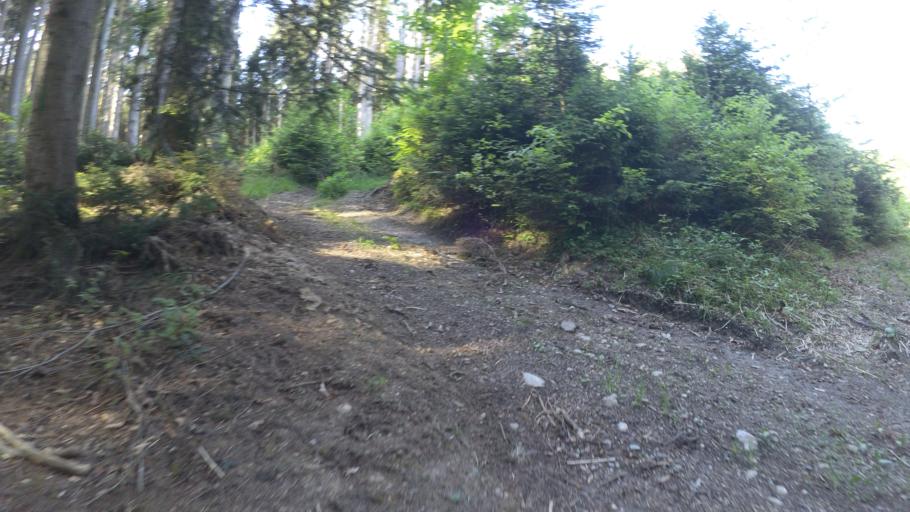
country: DE
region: Bavaria
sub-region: Upper Bavaria
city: Nussdorf
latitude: 47.8914
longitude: 12.5745
